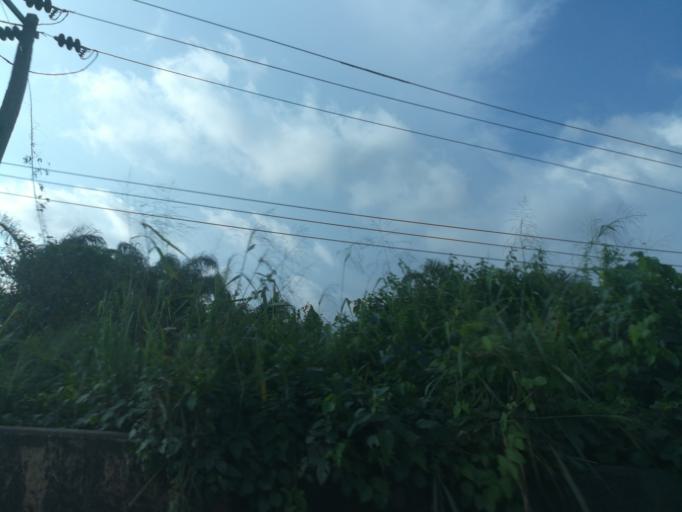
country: NG
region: Ogun
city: Ado Odo
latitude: 6.4915
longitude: 3.0772
